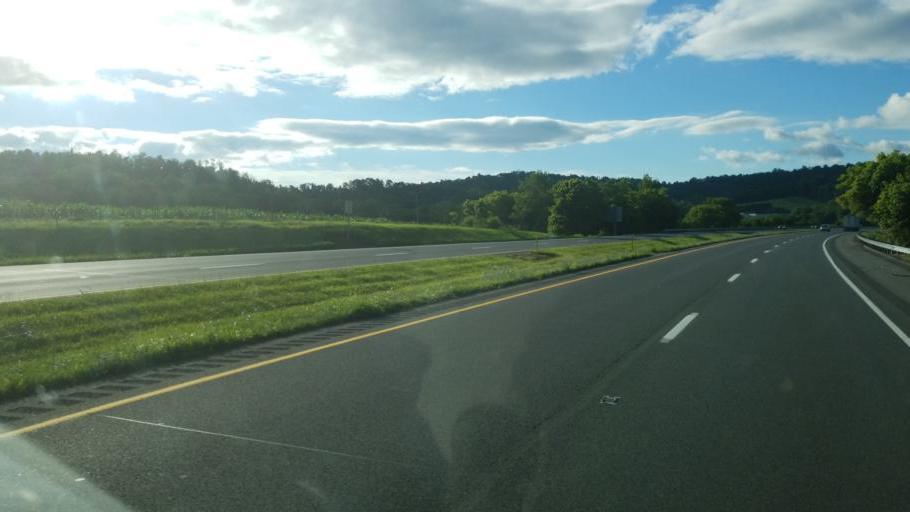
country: US
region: Maryland
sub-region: Washington County
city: Hancock
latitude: 39.7542
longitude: -78.1856
